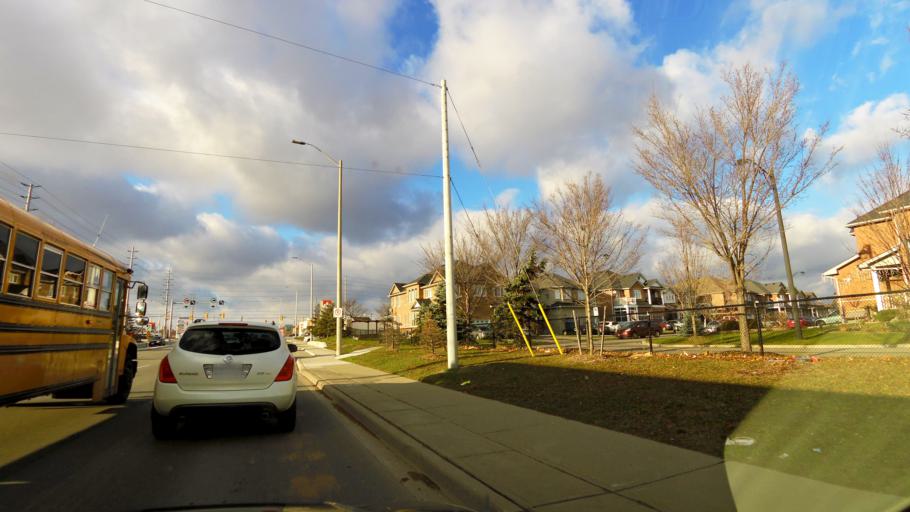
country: CA
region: Ontario
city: Brampton
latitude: 43.6356
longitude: -79.7154
